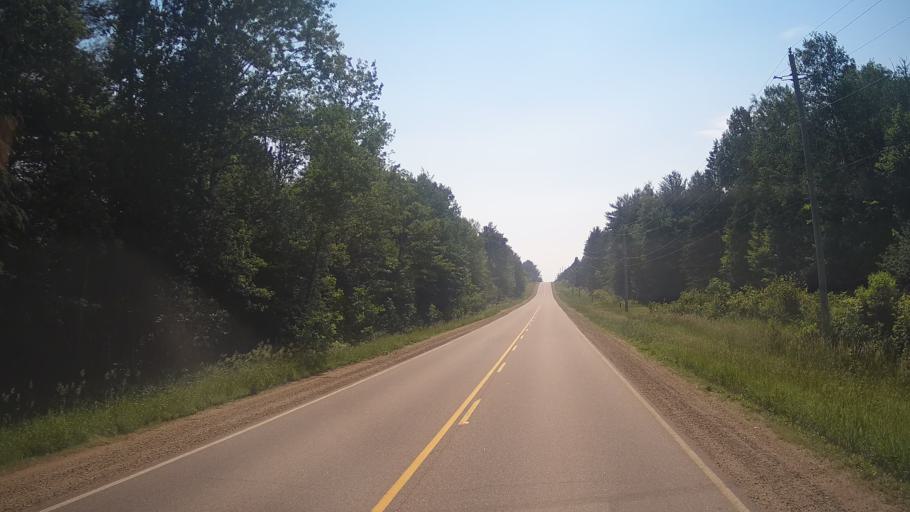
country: CA
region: Ontario
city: Pembroke
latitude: 45.6215
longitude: -77.1600
